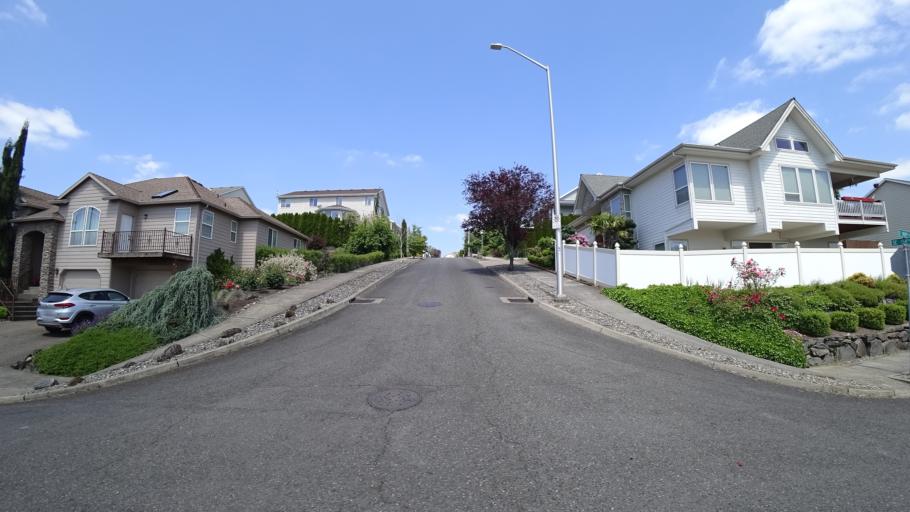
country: US
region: Oregon
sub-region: Clackamas County
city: Happy Valley
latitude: 45.4703
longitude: -122.5049
